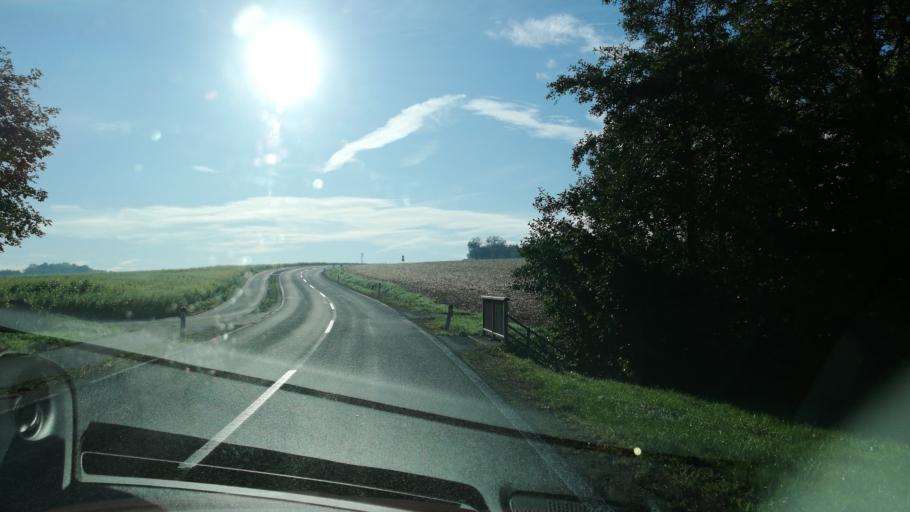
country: AT
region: Upper Austria
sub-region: Politischer Bezirk Steyr-Land
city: Waldneukirchen
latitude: 48.0119
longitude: 14.2440
